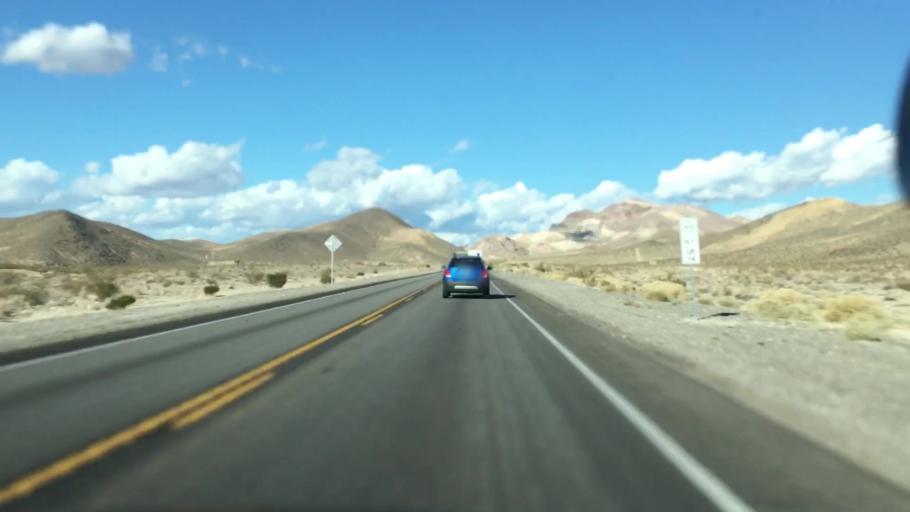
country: US
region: Nevada
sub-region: Nye County
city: Beatty
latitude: 36.8704
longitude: -116.7553
